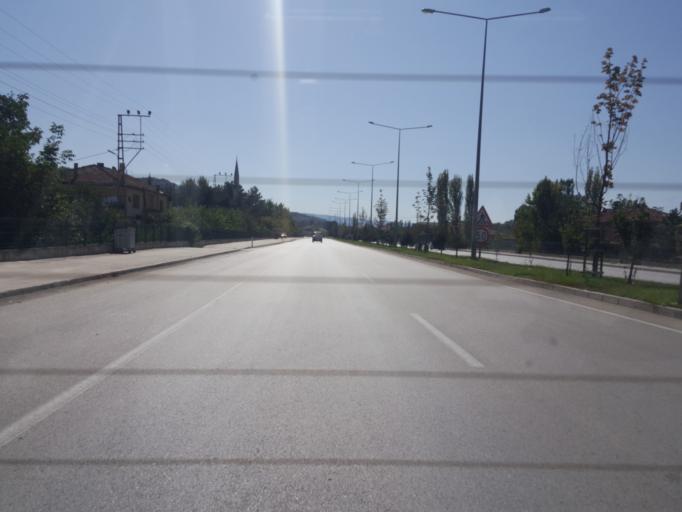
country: TR
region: Amasya
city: Amasya
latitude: 40.5969
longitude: 35.8054
